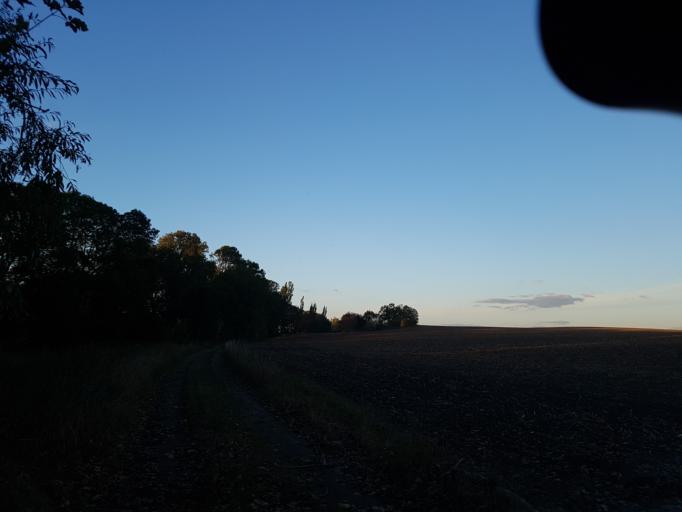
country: DE
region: Saxony
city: Oschatz
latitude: 51.2903
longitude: 13.1576
